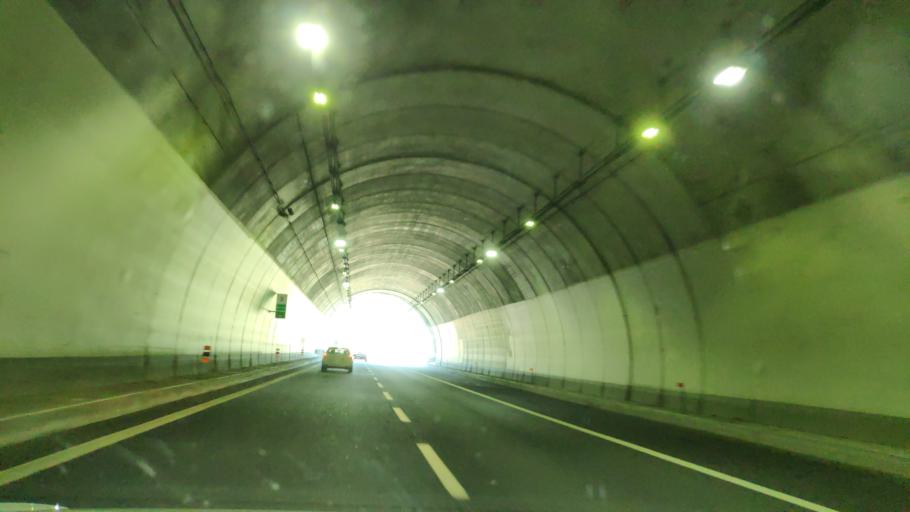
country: IT
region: Emilia-Romagna
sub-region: Provincia di Bologna
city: Grizzana
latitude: 44.2845
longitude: 11.2014
